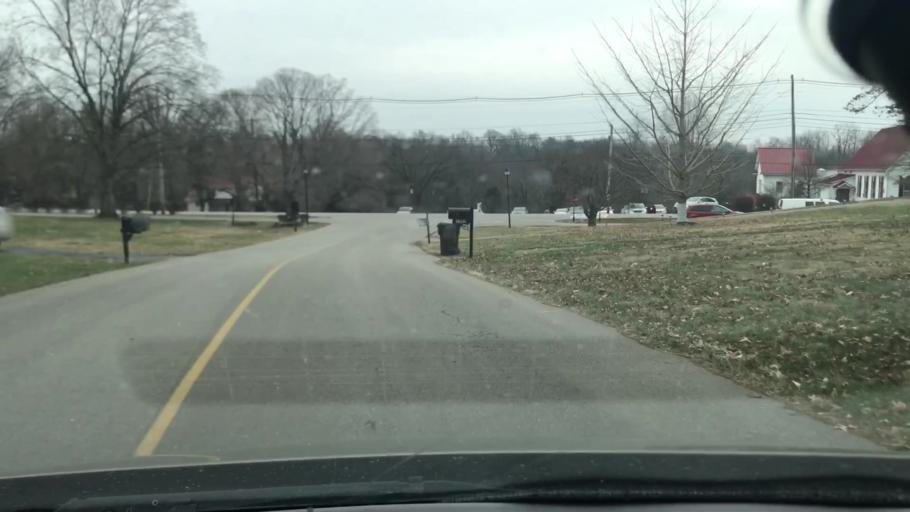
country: US
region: Kentucky
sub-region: Jefferson County
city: Barbourmeade
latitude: 38.2945
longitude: -85.6045
